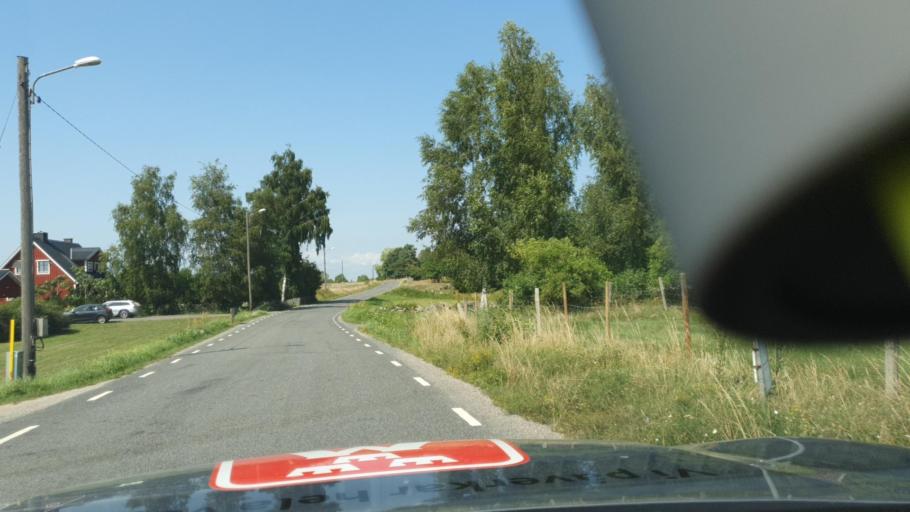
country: SE
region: Skane
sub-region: Kristianstads Kommun
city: Fjalkinge
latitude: 56.0679
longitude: 14.3622
